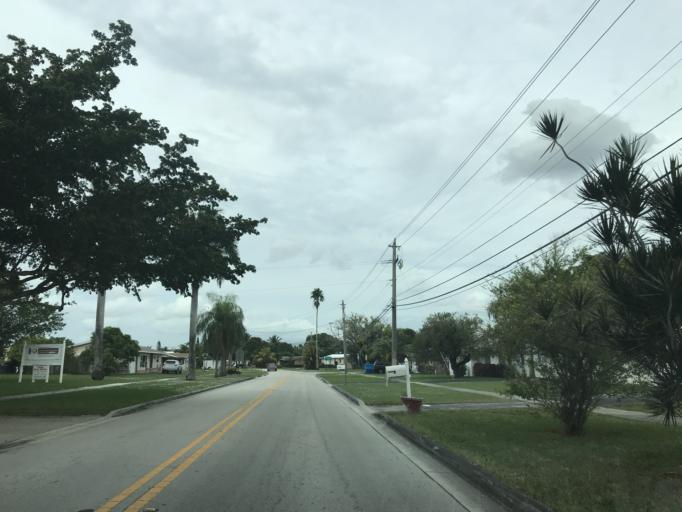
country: US
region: Florida
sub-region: Broward County
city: Margate
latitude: 26.2505
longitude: -80.2119
